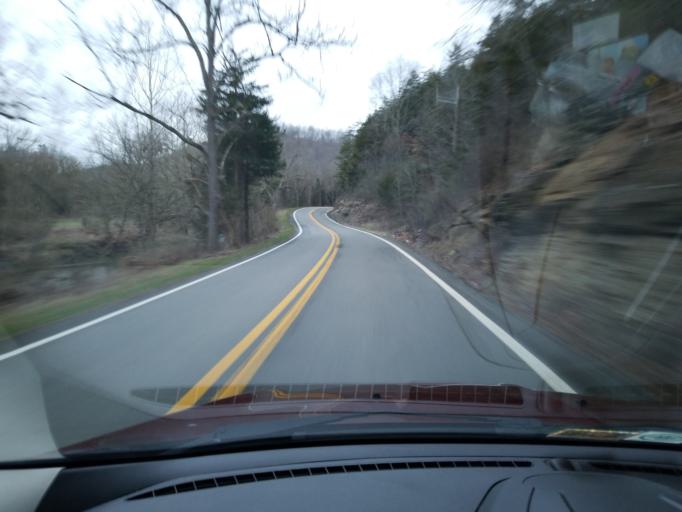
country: US
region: West Virginia
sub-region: Monroe County
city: Union
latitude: 37.5472
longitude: -80.5866
